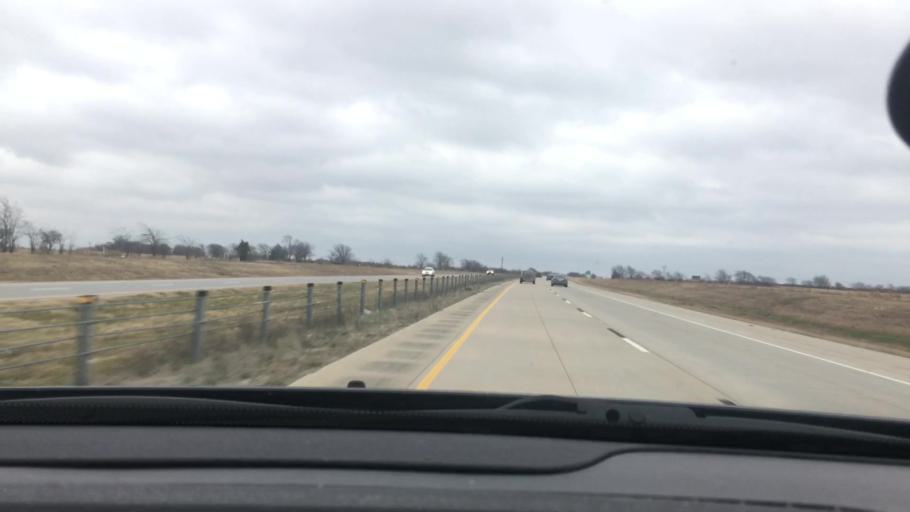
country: US
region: Oklahoma
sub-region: Bryan County
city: Durant
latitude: 34.0804
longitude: -96.3358
